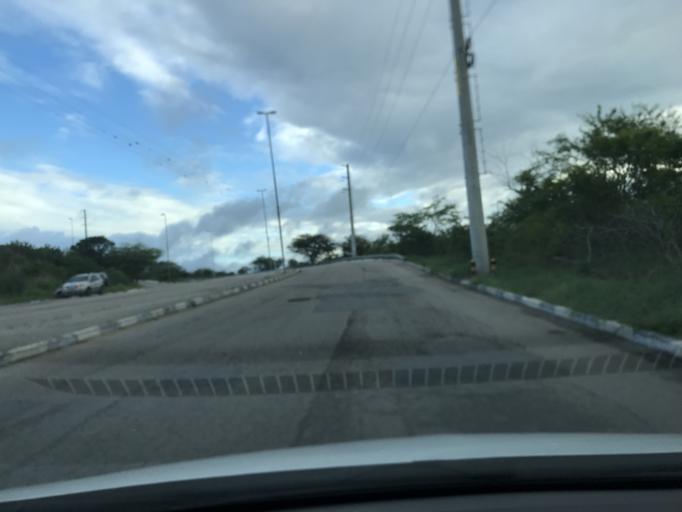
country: BR
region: Pernambuco
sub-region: Caruaru
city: Caruaru
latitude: -8.3050
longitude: -35.9417
